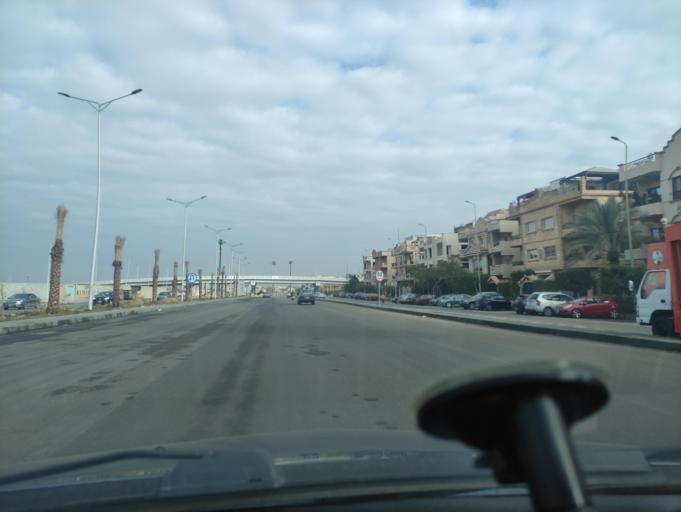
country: EG
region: Muhafazat al Qalyubiyah
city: Al Khankah
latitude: 30.0492
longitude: 31.4425
